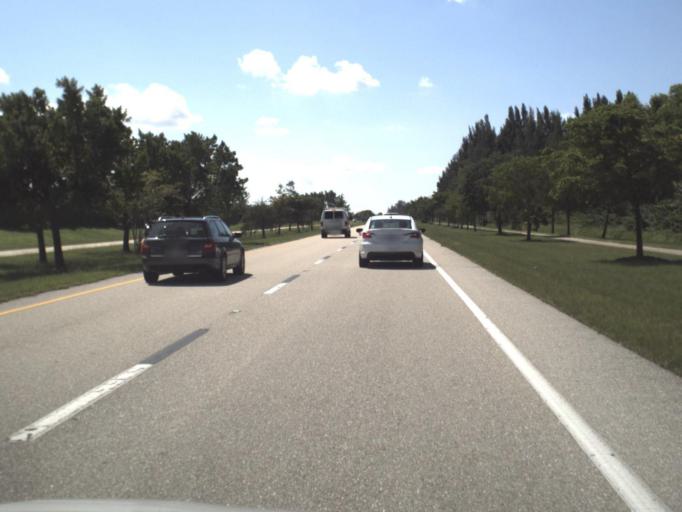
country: US
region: Florida
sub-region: Lee County
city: Pine Island Center
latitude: 26.6298
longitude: -82.0407
